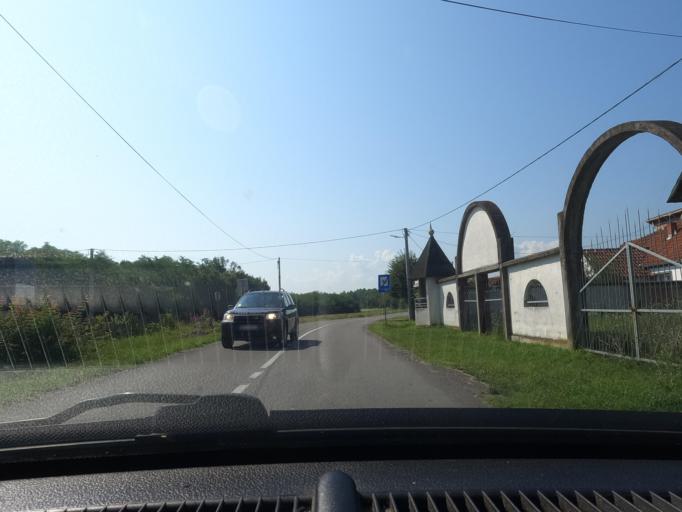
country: RS
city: Kozjak
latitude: 44.5552
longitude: 19.2959
